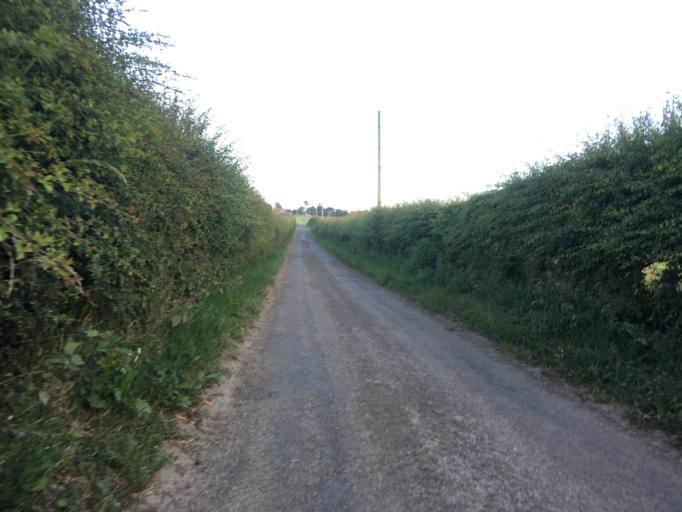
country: GB
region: England
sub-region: Northumberland
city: North Sunderland
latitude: 55.5914
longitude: -1.6865
